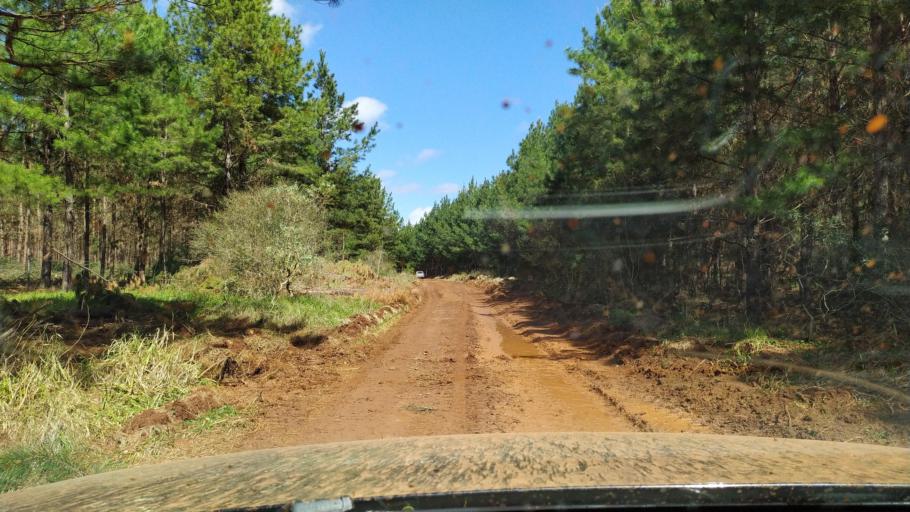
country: AR
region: Corrientes
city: Santo Tome
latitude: -28.4042
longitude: -56.0137
